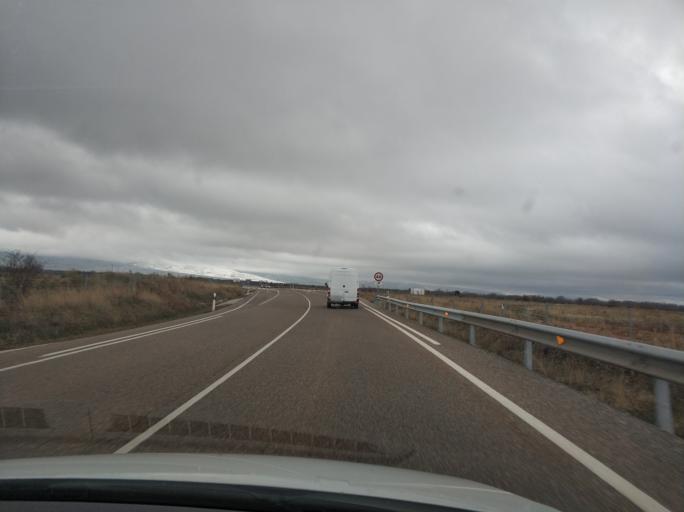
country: ES
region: Castille and Leon
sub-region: Provincia de Segovia
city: Riaza
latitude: 41.2826
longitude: -3.4940
